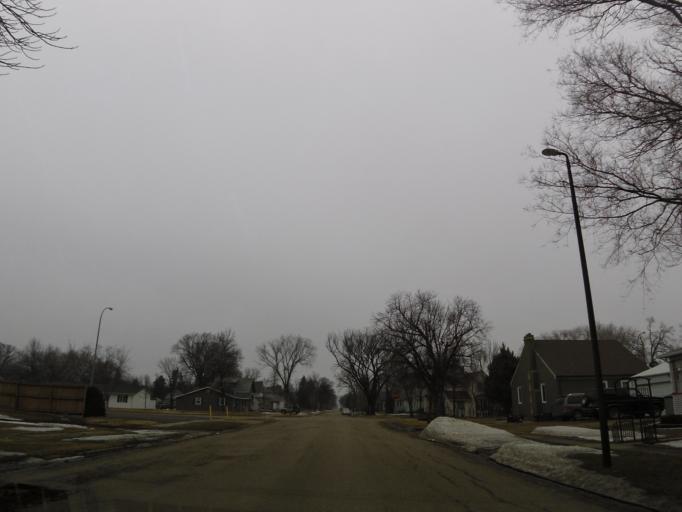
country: US
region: North Dakota
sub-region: Walsh County
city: Grafton
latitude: 48.4119
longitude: -97.4128
